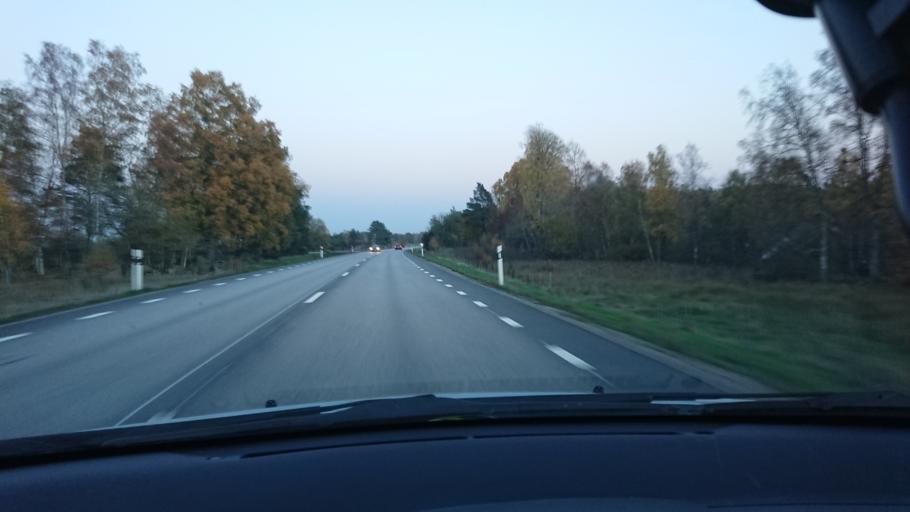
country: SE
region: Kronoberg
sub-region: Markaryds Kommun
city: Stromsnasbruk
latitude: 56.7562
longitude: 13.7104
